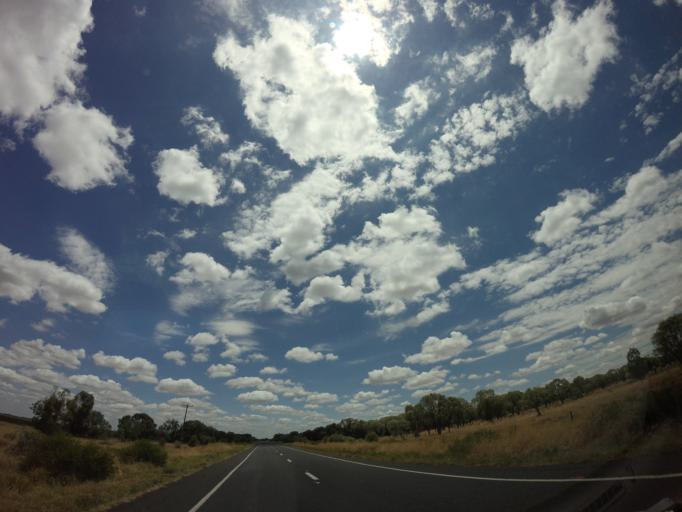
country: AU
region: New South Wales
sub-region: Moree Plains
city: Boggabilla
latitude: -28.9077
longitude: 150.1341
